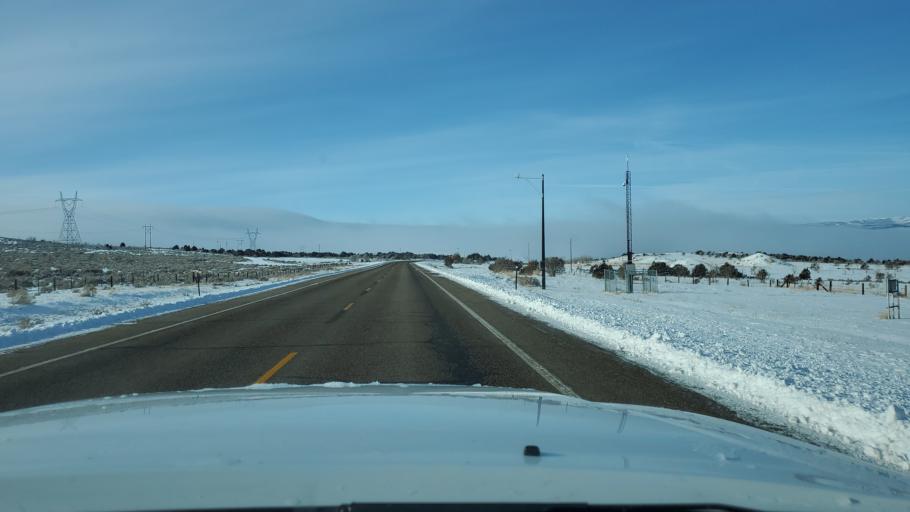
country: US
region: Colorado
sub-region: Rio Blanco County
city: Rangely
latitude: 40.3704
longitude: -108.3884
